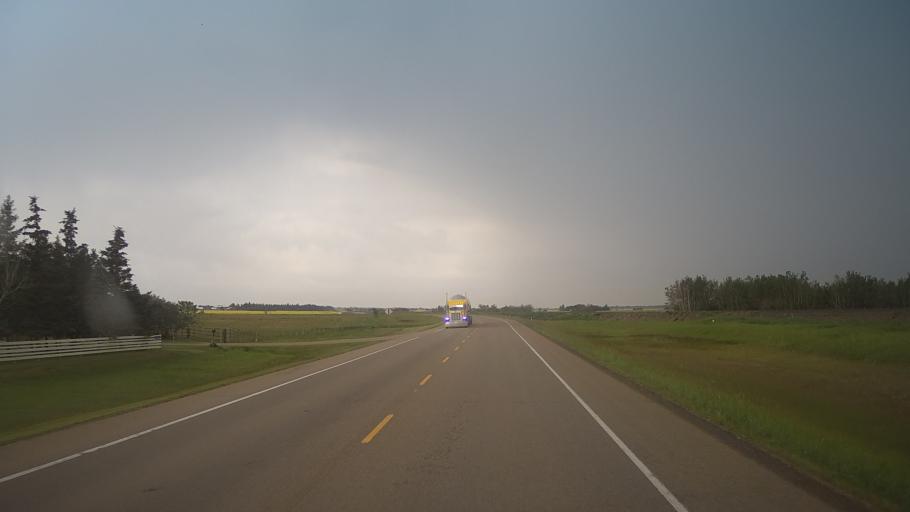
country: CA
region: Alberta
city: Tofield
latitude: 53.3302
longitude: -112.5762
